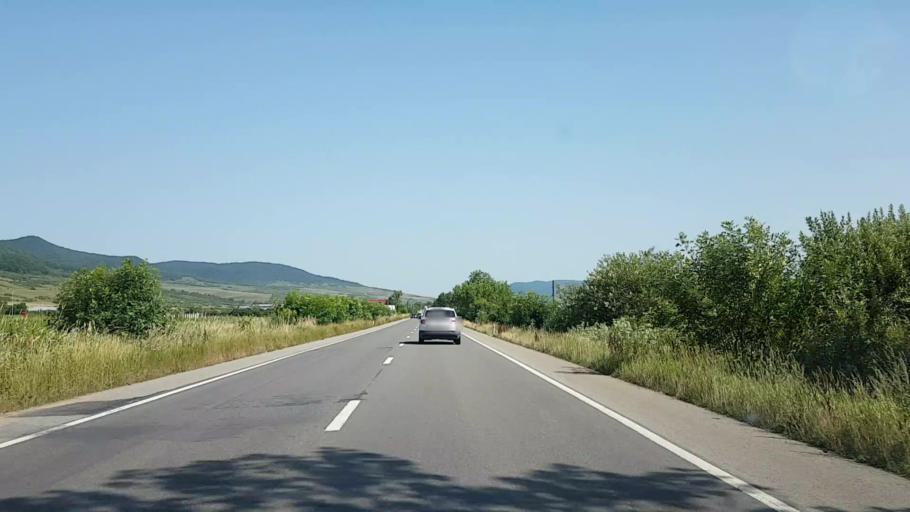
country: RO
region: Bistrita-Nasaud
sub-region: Comuna Sieu-Magherus
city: Sieu-Magherus
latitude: 47.1033
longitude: 24.3563
